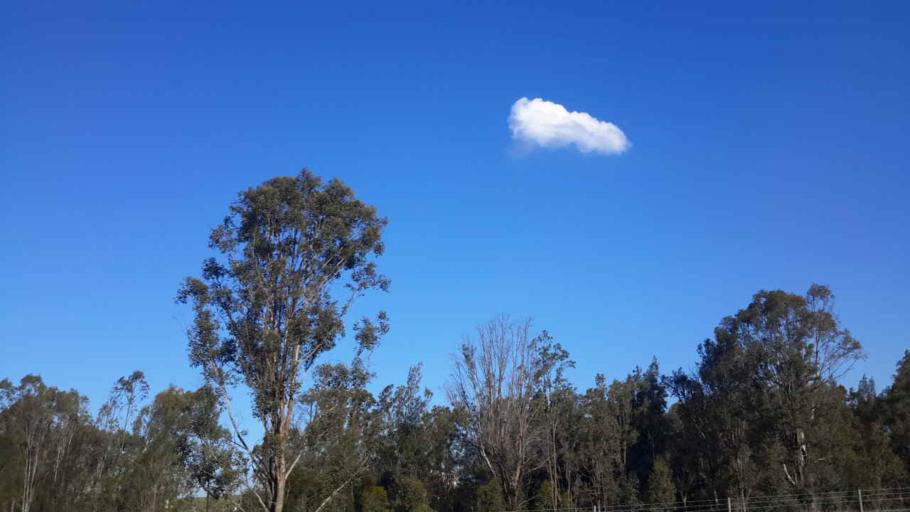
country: AU
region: New South Wales
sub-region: Penrith Municipality
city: Glenmore Park
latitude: -33.8102
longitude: 150.6941
